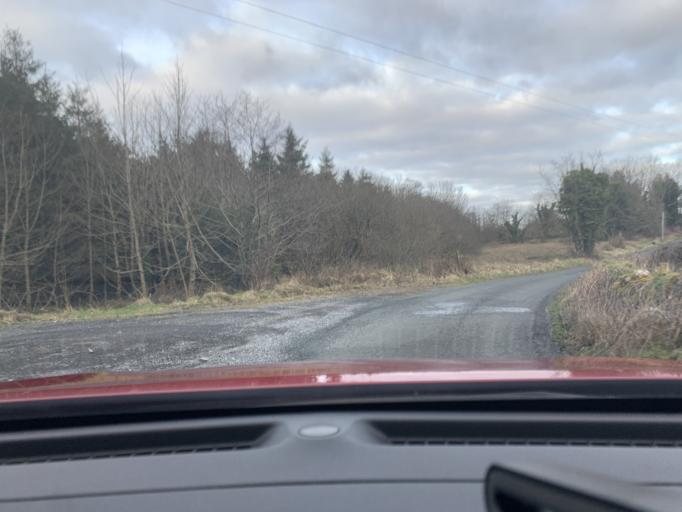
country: IE
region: Connaught
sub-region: Roscommon
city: Ballaghaderreen
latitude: 53.9777
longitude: -8.5592
